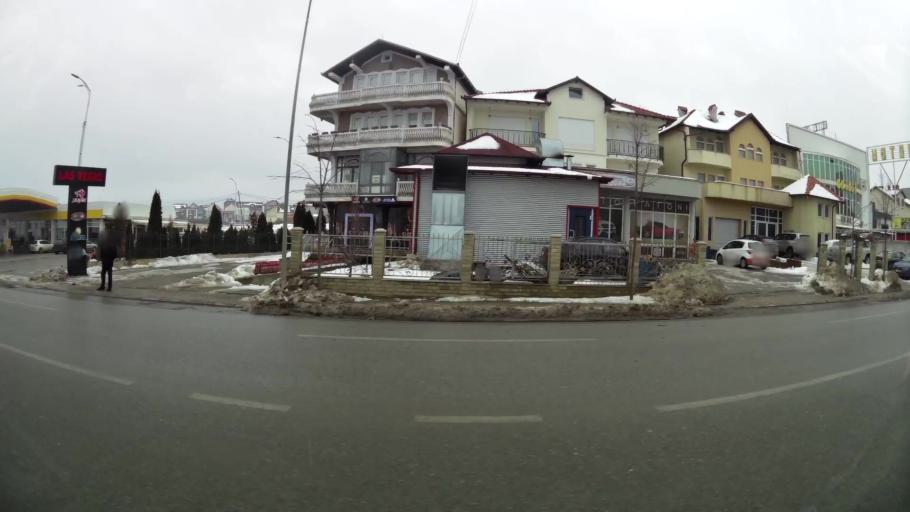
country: XK
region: Pristina
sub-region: Komuna e Prishtines
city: Pristina
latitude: 42.6971
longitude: 21.1597
